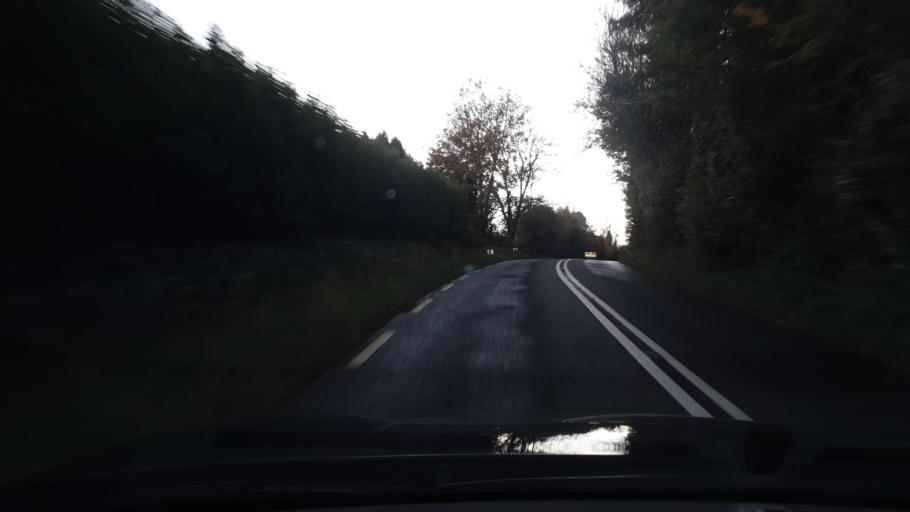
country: IE
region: Leinster
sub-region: Lu
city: Tullyallen
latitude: 53.7229
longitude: -6.4310
